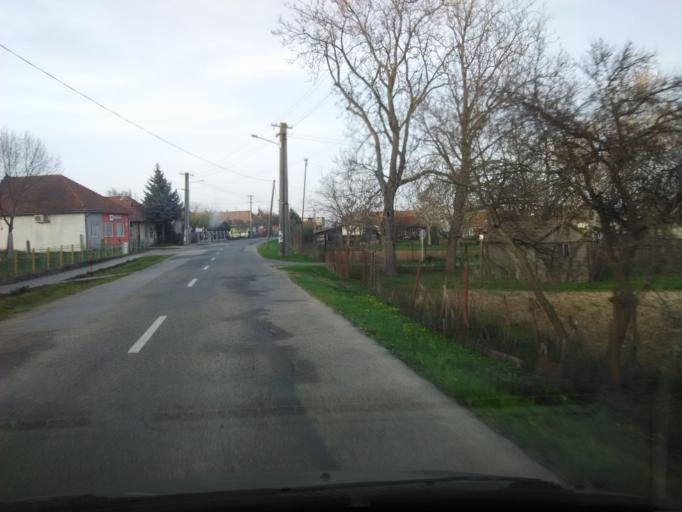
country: SK
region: Nitriansky
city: Tlmace
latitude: 48.1852
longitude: 18.4571
